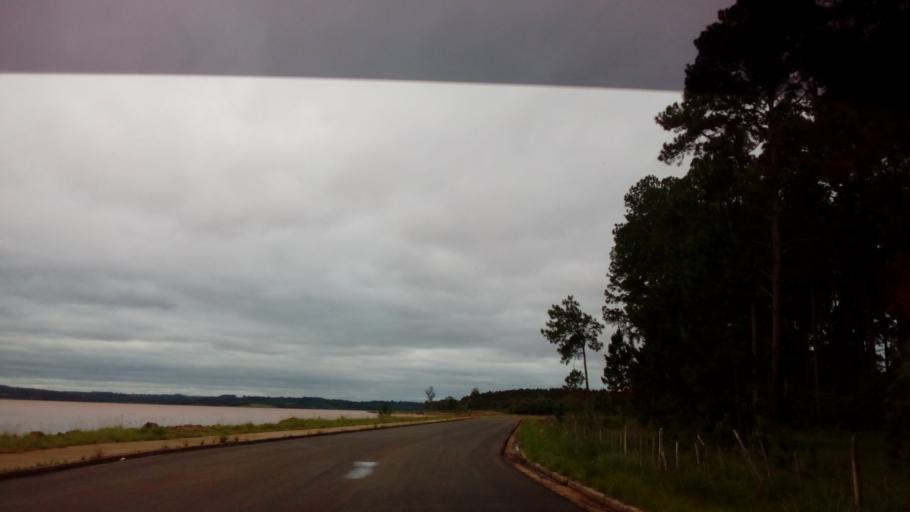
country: AR
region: Misiones
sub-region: Departamento de Candelaria
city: Candelaria
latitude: -27.4558
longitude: -55.7894
